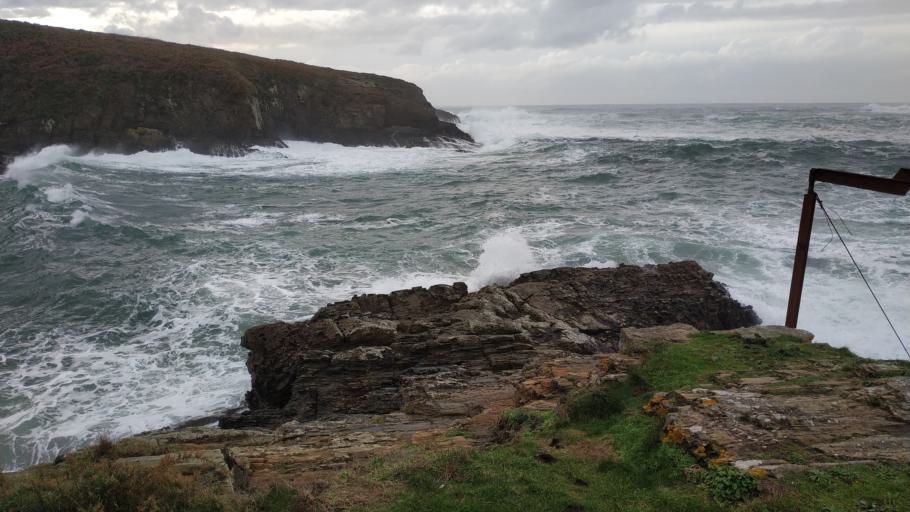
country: ES
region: Galicia
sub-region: Provincia da Coruna
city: Oleiros
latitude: 43.4008
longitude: -8.3304
